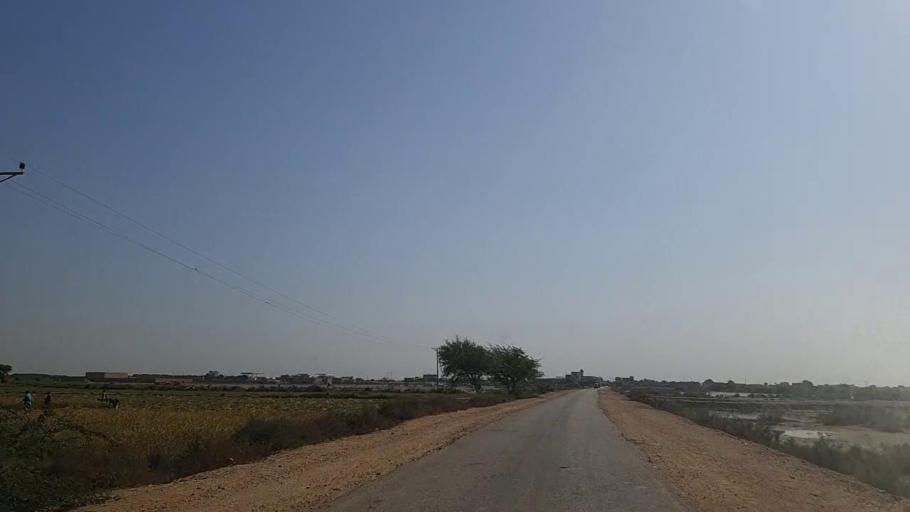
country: PK
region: Sindh
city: Mirpur Batoro
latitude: 24.6239
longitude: 68.2947
